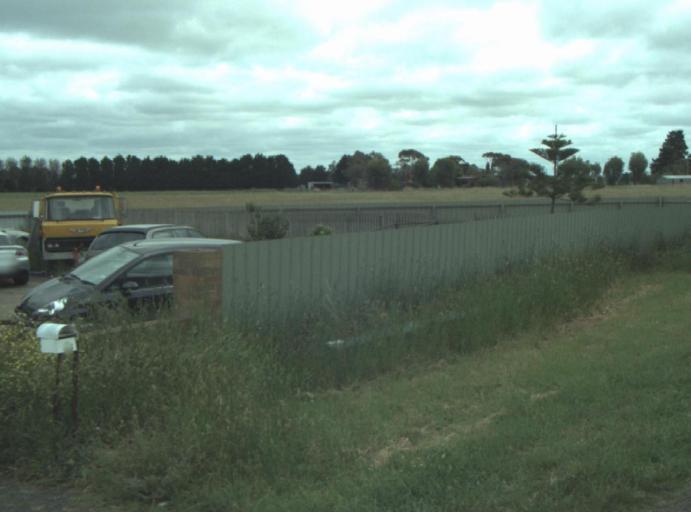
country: AU
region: Victoria
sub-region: Greater Geelong
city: Bell Post Hill
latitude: -38.0599
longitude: 144.3218
